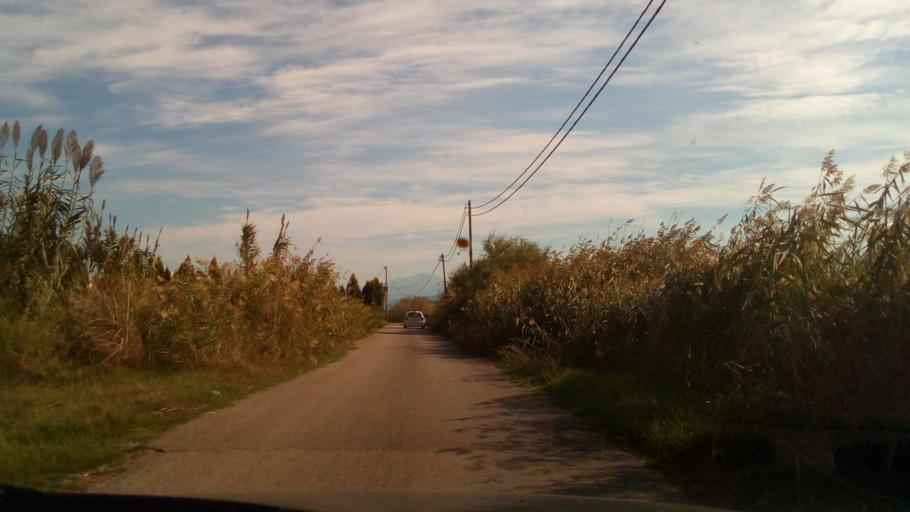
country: GR
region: West Greece
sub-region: Nomos Aitolias kai Akarnanias
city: Nafpaktos
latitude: 38.4017
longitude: 21.9235
